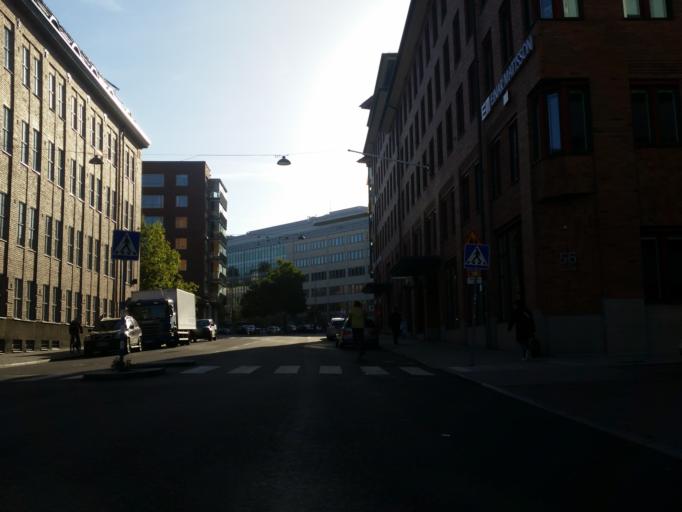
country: SE
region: Stockholm
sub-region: Stockholms Kommun
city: Arsta
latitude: 59.3116
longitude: 18.0582
